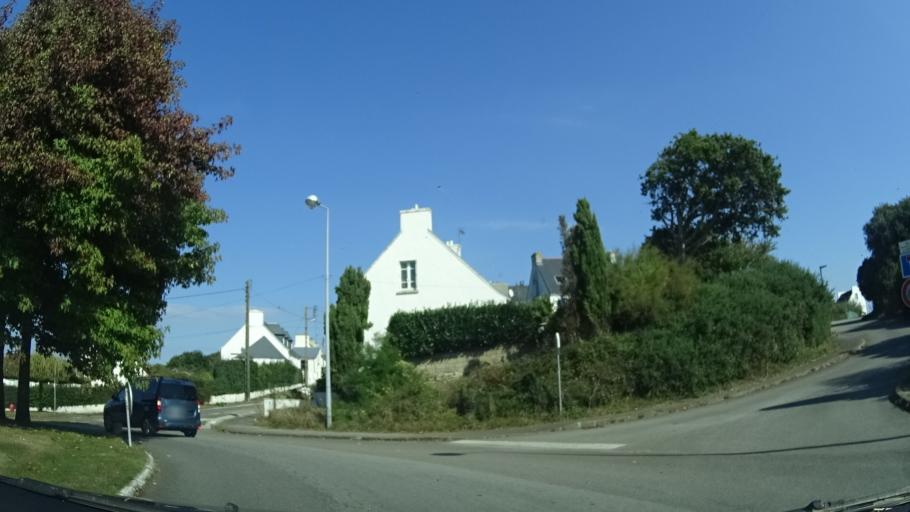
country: FR
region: Brittany
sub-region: Departement du Finistere
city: Douarnenez
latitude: 48.0925
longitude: -4.3454
